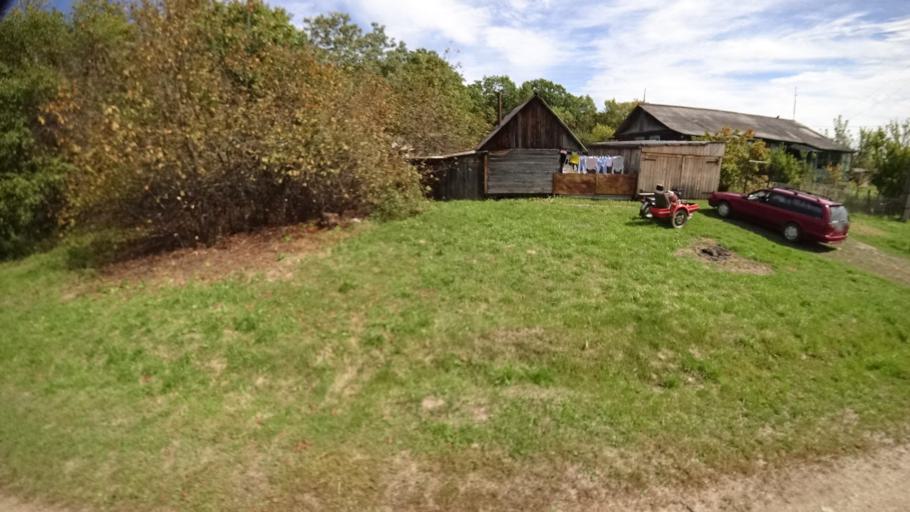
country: RU
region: Primorskiy
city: Yakovlevka
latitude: 44.6490
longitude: 133.5879
